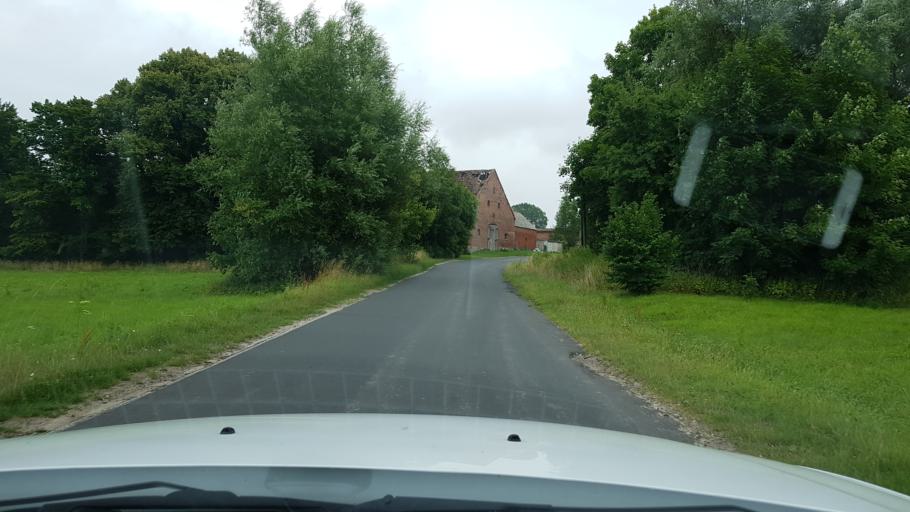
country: PL
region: West Pomeranian Voivodeship
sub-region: Powiat slawienski
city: Slawno
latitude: 54.4902
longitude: 16.5804
